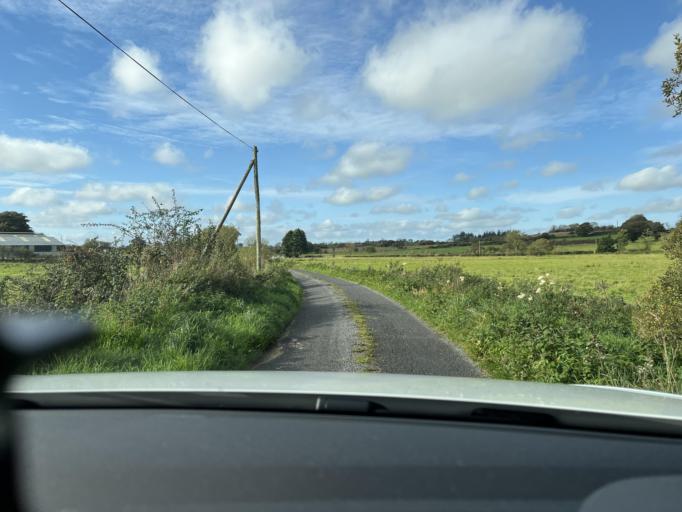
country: IE
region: Connaught
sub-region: Sligo
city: Ballymote
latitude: 54.0722
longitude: -8.4297
